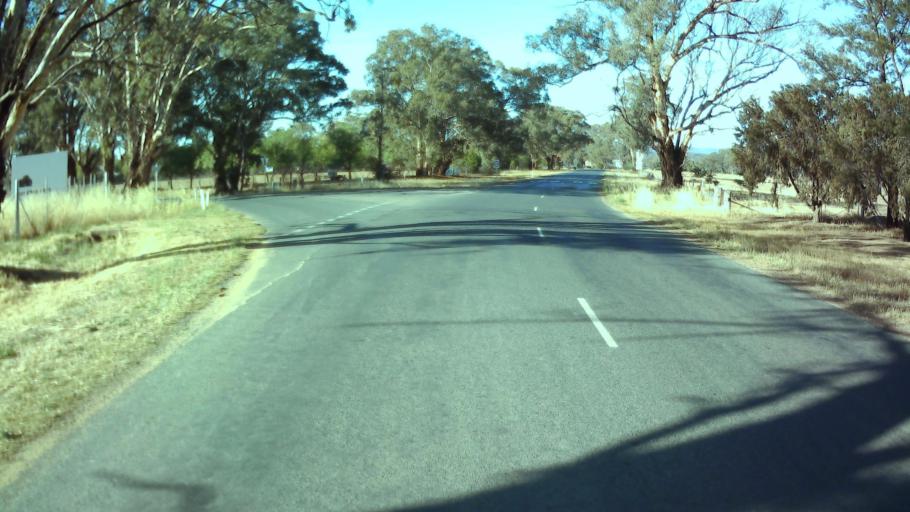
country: AU
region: New South Wales
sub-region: Weddin
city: Grenfell
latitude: -33.9013
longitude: 148.1517
